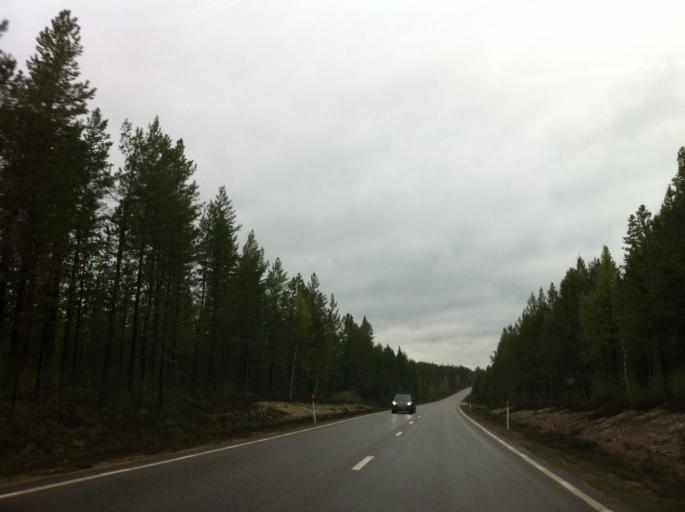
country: SE
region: Jaemtland
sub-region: Harjedalens Kommun
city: Sveg
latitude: 62.1094
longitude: 14.1905
